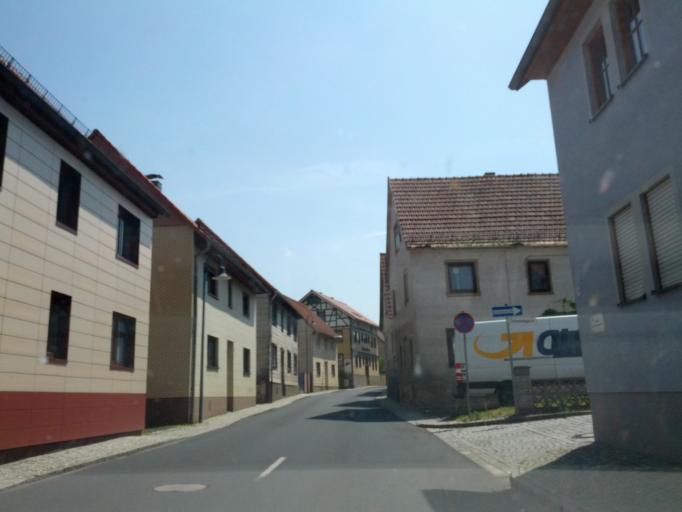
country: DE
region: Thuringia
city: Kaltennordheim
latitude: 50.6256
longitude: 10.1576
